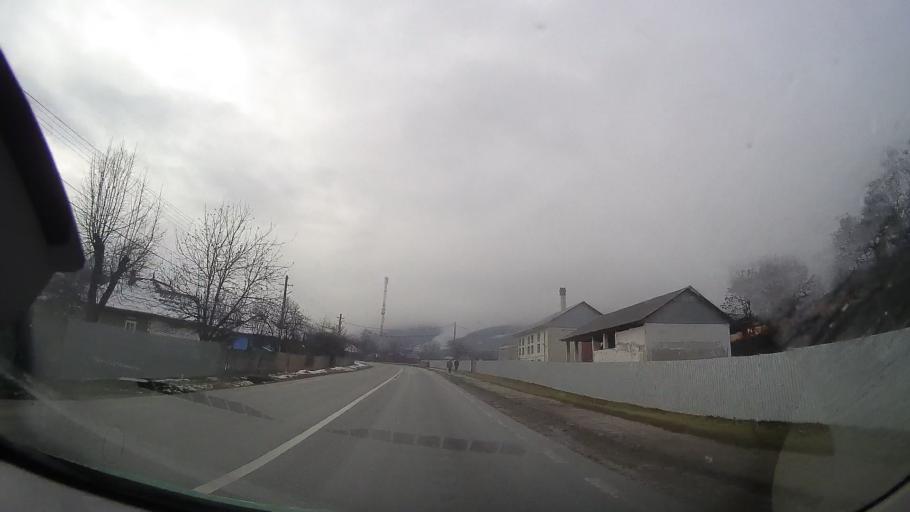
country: RO
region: Neamt
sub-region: Comuna Tasca
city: Tasca
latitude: 46.8966
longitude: 26.0271
